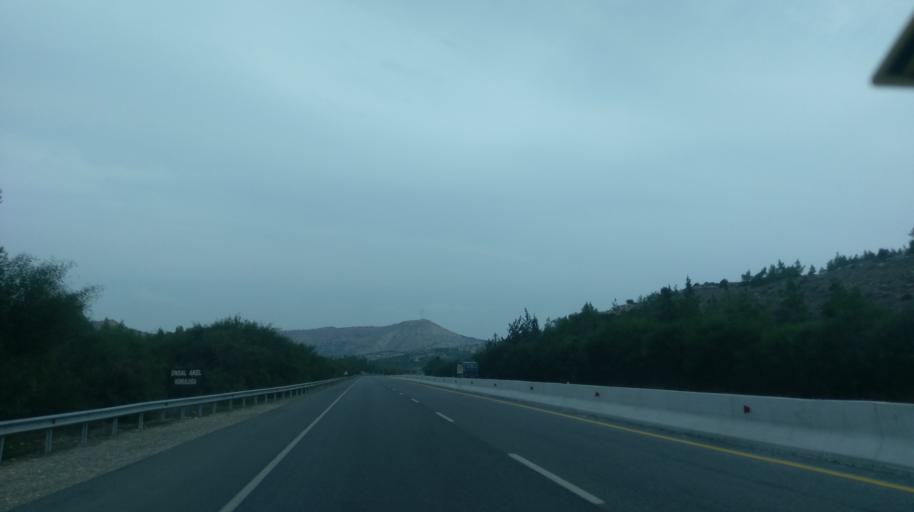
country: CY
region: Lefkosia
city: Akaki
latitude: 35.1998
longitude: 33.1149
